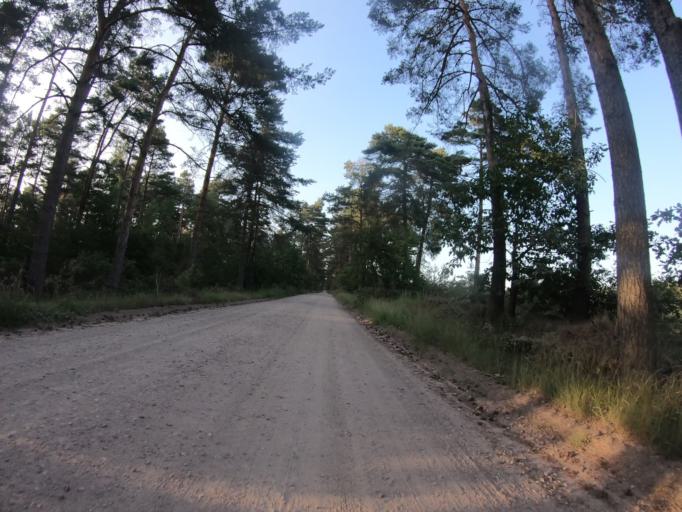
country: DE
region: Lower Saxony
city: Wagenhoff
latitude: 52.5392
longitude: 10.4961
